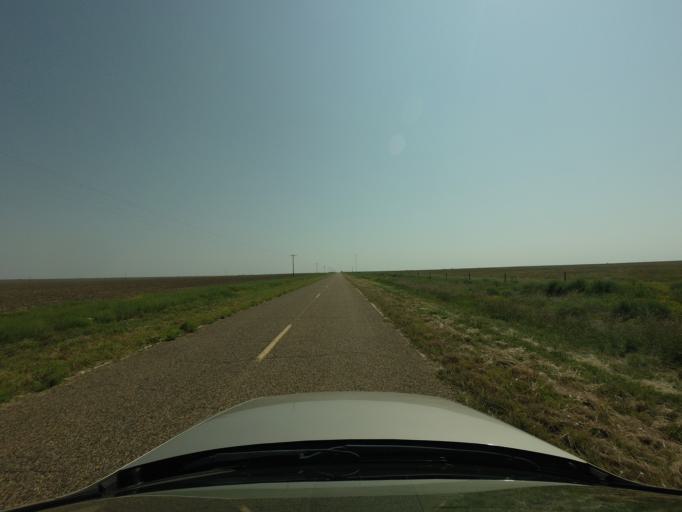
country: US
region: New Mexico
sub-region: Curry County
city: Cannon Air Force Base
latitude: 34.6336
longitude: -103.6135
